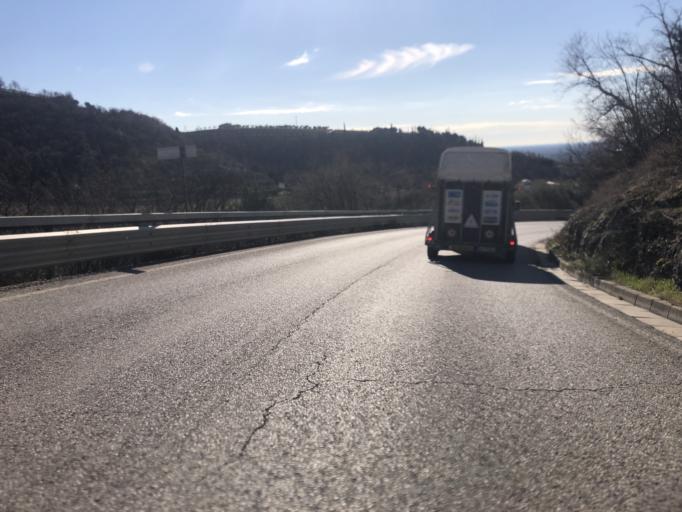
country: IT
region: Veneto
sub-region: Provincia di Verona
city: Sant'Ambrogio di Valpollicella
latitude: 45.5300
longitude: 10.8386
